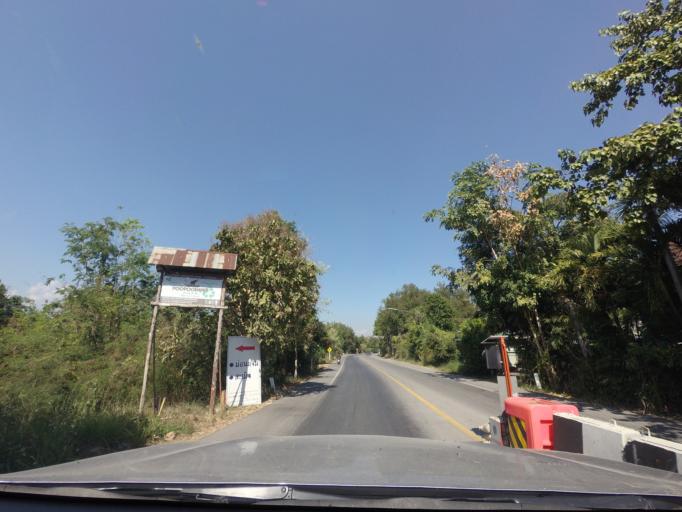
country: TH
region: Chiang Mai
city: San Sai
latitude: 18.9145
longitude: 98.9411
